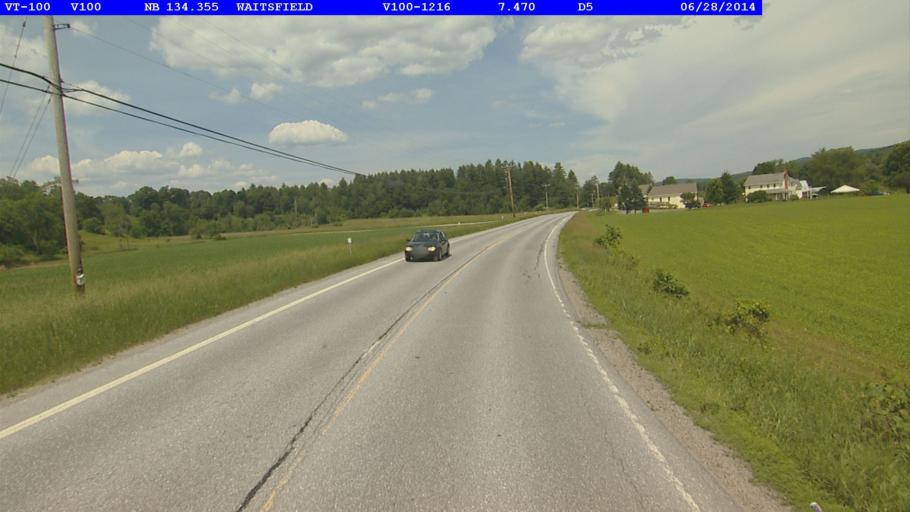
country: US
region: Vermont
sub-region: Washington County
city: Waterbury
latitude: 44.2339
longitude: -72.7815
